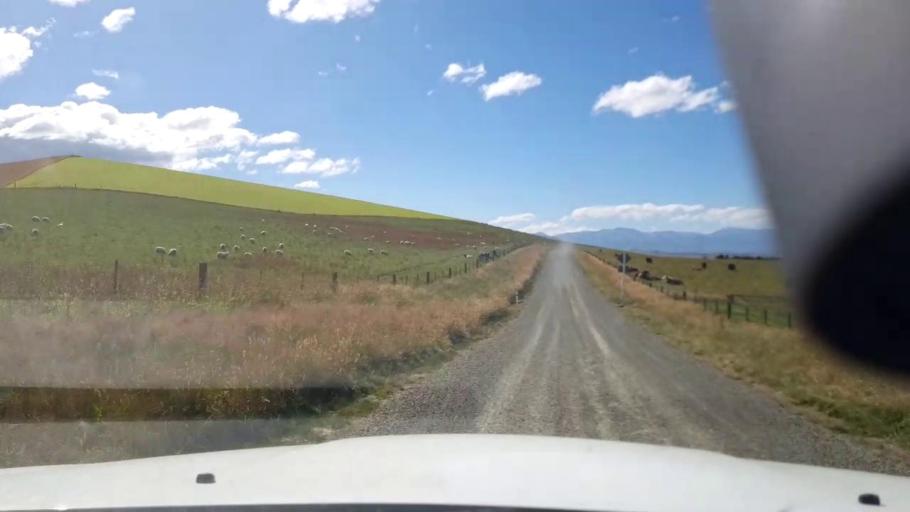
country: NZ
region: Canterbury
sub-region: Timaru District
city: Pleasant Point
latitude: -44.3197
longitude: 170.8760
